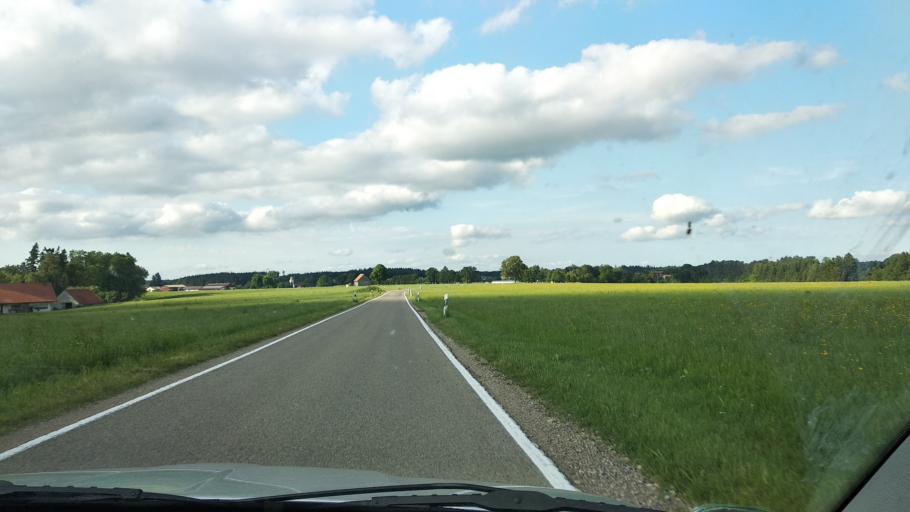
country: DE
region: Baden-Wuerttemberg
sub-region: Tuebingen Region
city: Rot an der Rot
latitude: 47.9661
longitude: 10.0413
